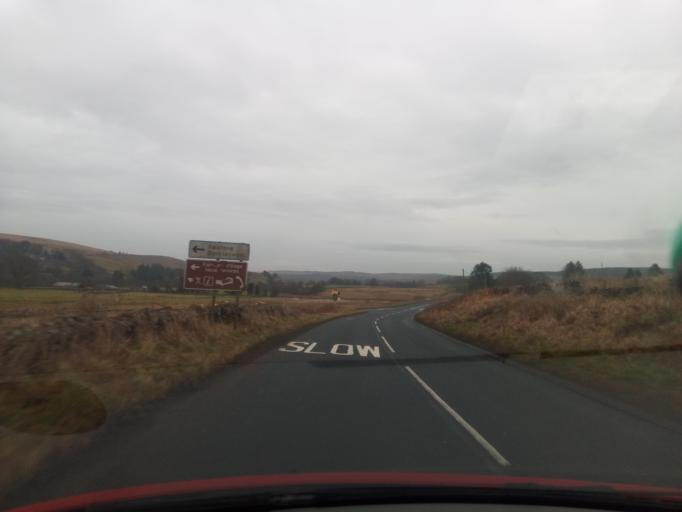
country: GB
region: England
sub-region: Northumberland
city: Rochester
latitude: 55.1758
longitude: -2.4410
